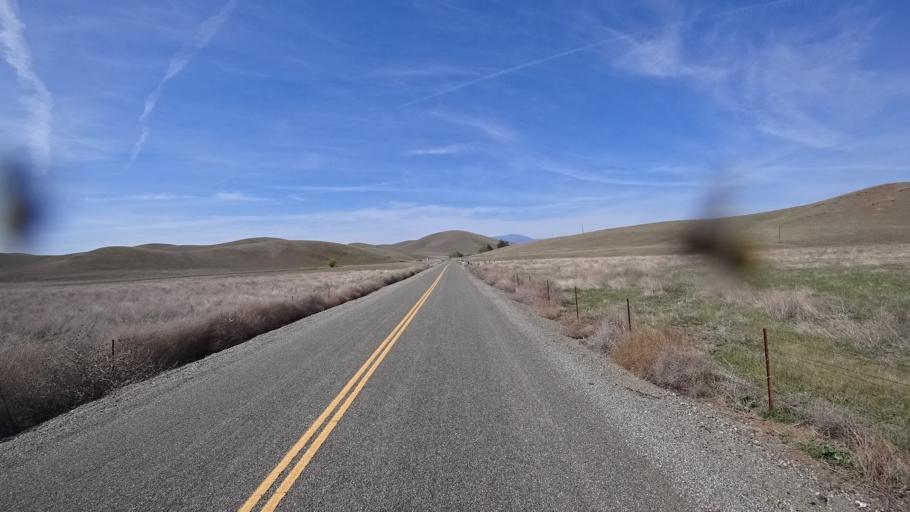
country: US
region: California
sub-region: Glenn County
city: Willows
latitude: 39.5527
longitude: -122.3603
